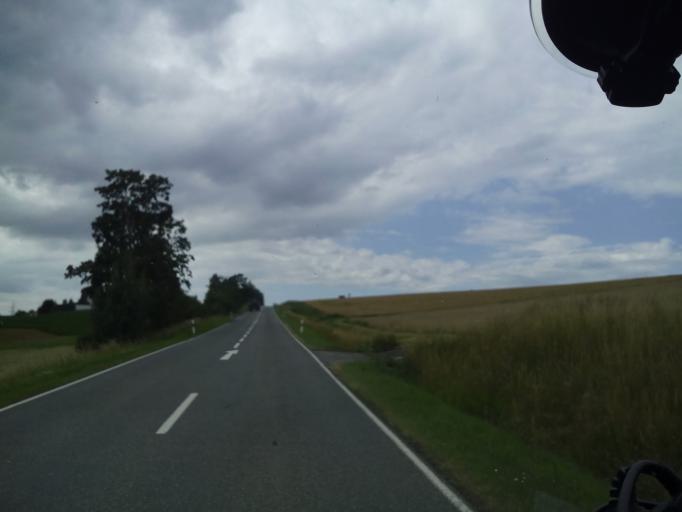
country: DE
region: Bavaria
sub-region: Upper Franconia
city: Sonnefeld
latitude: 50.2392
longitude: 11.1169
